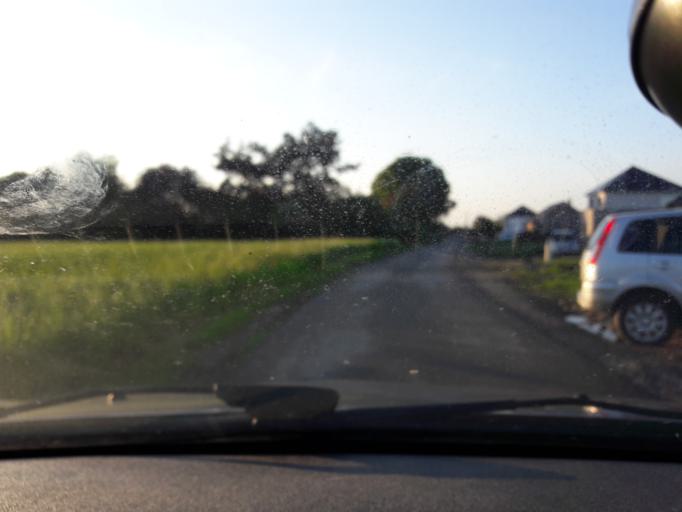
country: FR
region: Nord-Pas-de-Calais
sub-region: Departement du Nord
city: Recquignies
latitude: 50.2766
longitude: 4.0463
